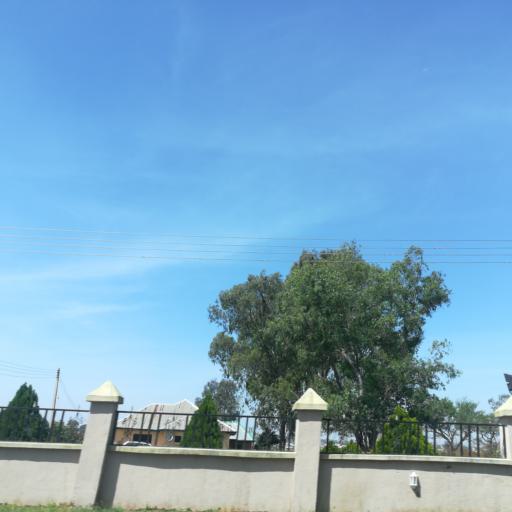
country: NG
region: Plateau
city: Bukuru
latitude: 9.7720
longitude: 8.8873
